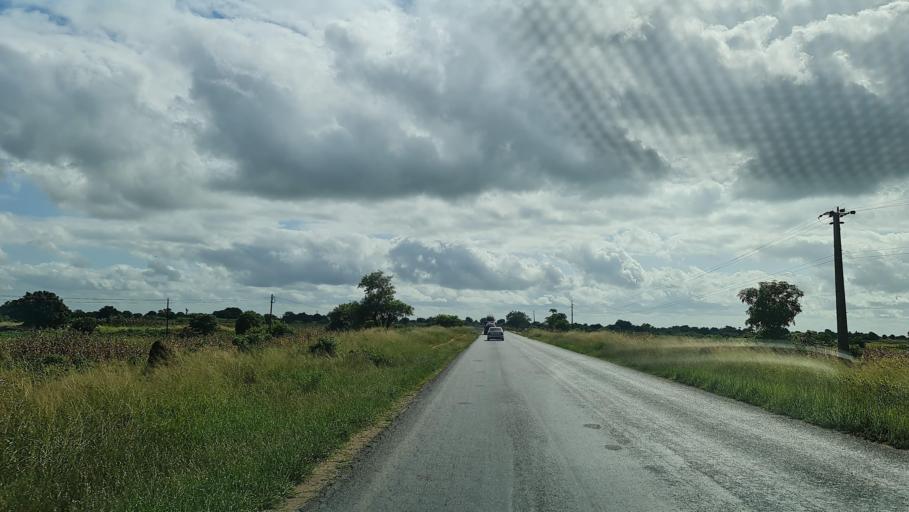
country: MZ
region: Gaza
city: Macia
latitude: -25.0908
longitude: 32.8397
